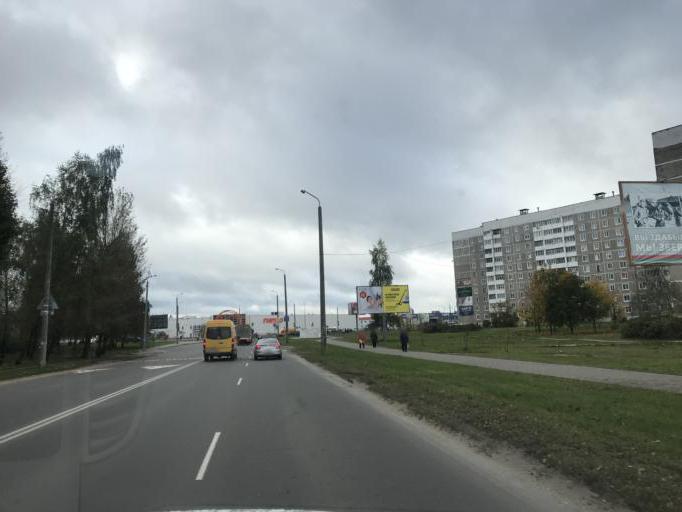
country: BY
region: Mogilev
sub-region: Mahilyowski Rayon
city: Veyno
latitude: 53.8746
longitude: 30.3653
